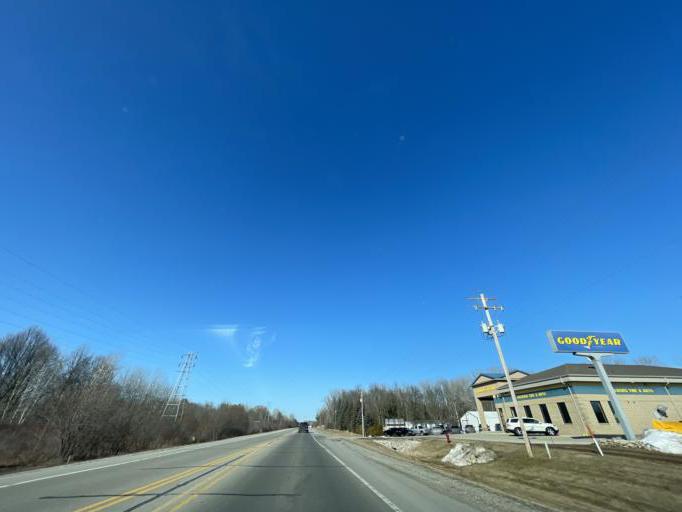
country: US
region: Wisconsin
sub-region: Brown County
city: Howard
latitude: 44.5935
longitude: -88.0779
